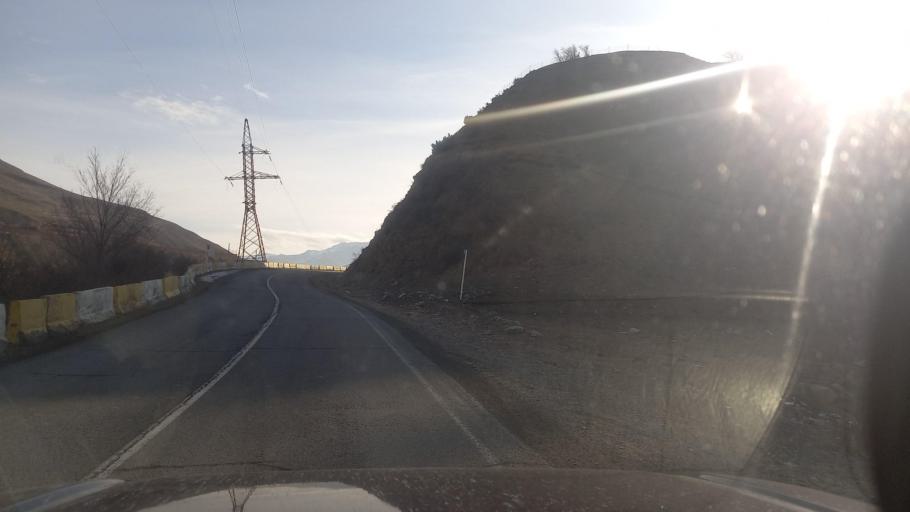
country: RU
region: Ingushetiya
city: Dzhayrakh
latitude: 42.8318
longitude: 44.6655
